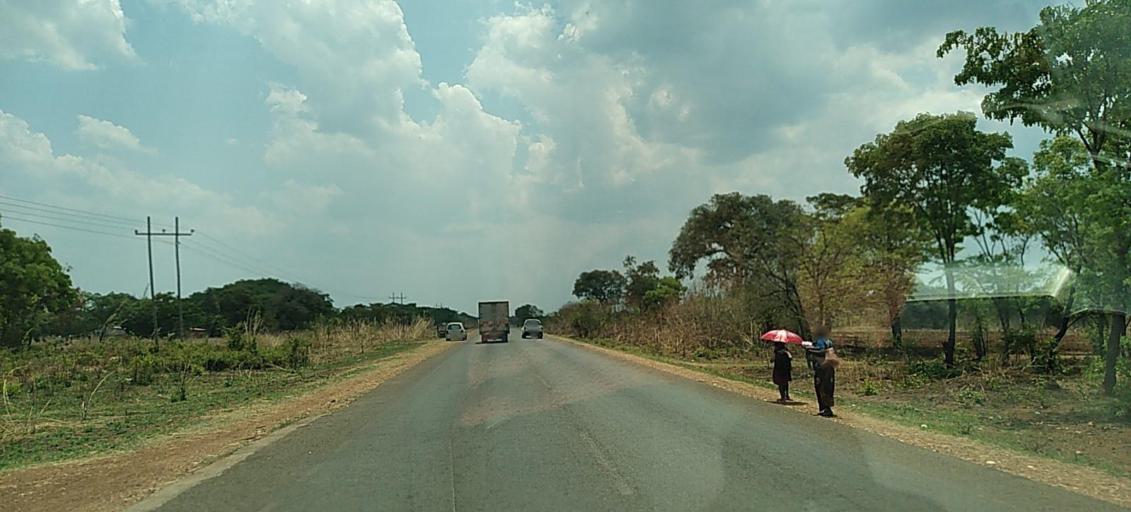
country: ZM
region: Copperbelt
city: Kalulushi
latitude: -12.8354
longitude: 27.9560
